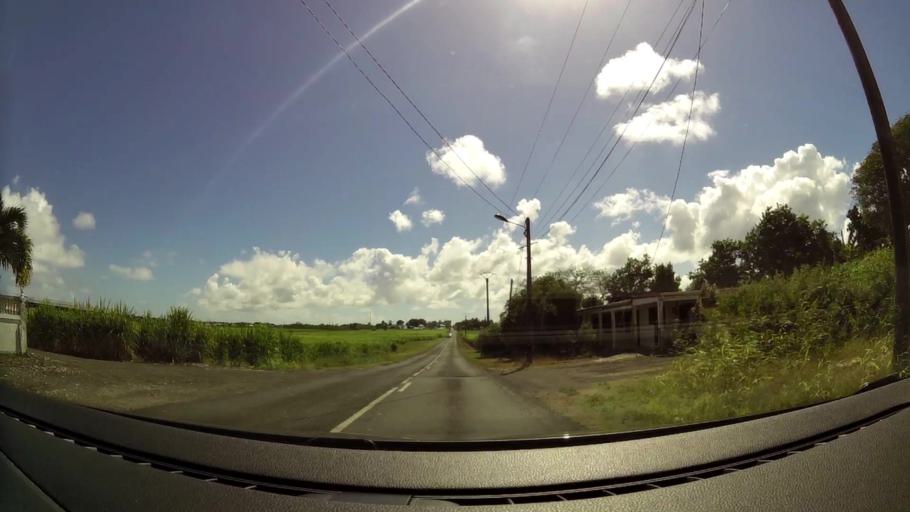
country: GP
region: Guadeloupe
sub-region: Guadeloupe
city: Petit-Canal
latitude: 16.4047
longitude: -61.4664
